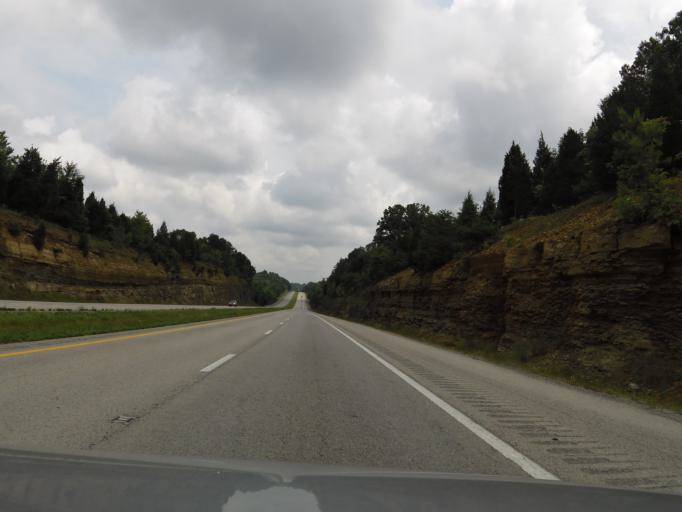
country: US
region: Kentucky
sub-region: Grayson County
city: Leitchfield
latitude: 37.5025
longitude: -86.1622
